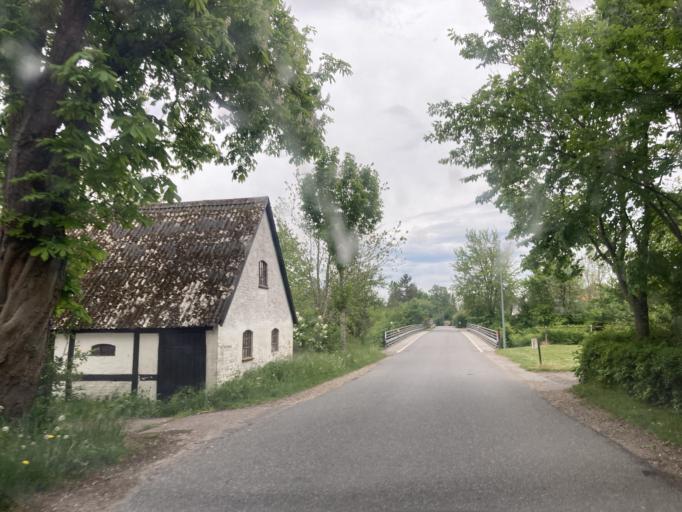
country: DK
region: Zealand
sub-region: Roskilde Kommune
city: Svogerslev
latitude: 55.6368
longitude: 11.9818
